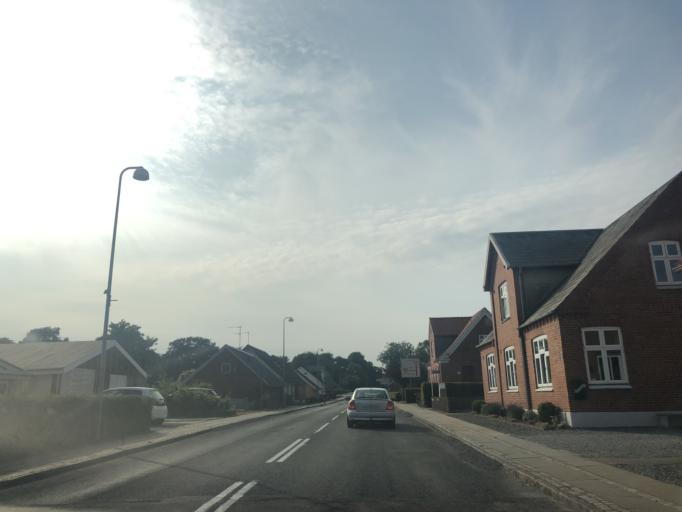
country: DK
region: Central Jutland
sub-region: Skive Kommune
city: Skive
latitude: 56.7021
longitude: 8.9839
